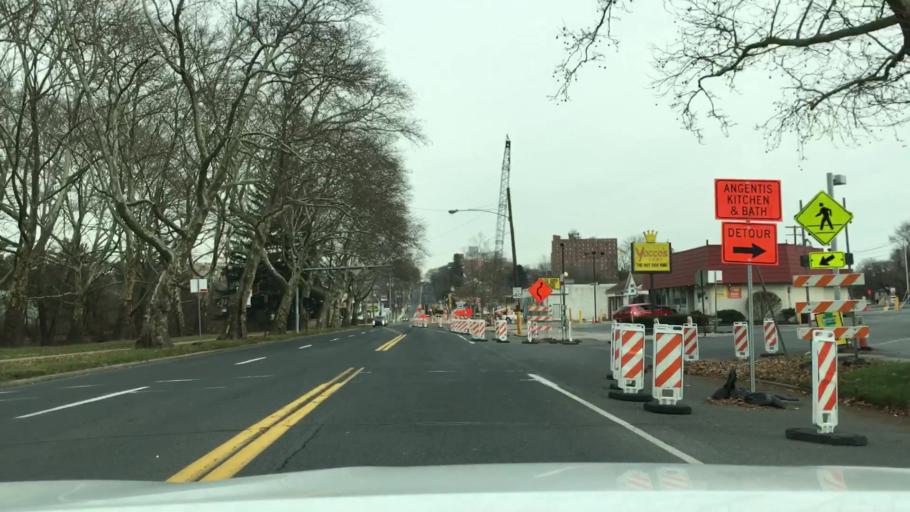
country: US
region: Pennsylvania
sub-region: Lehigh County
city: Allentown
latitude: 40.5937
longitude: -75.5025
